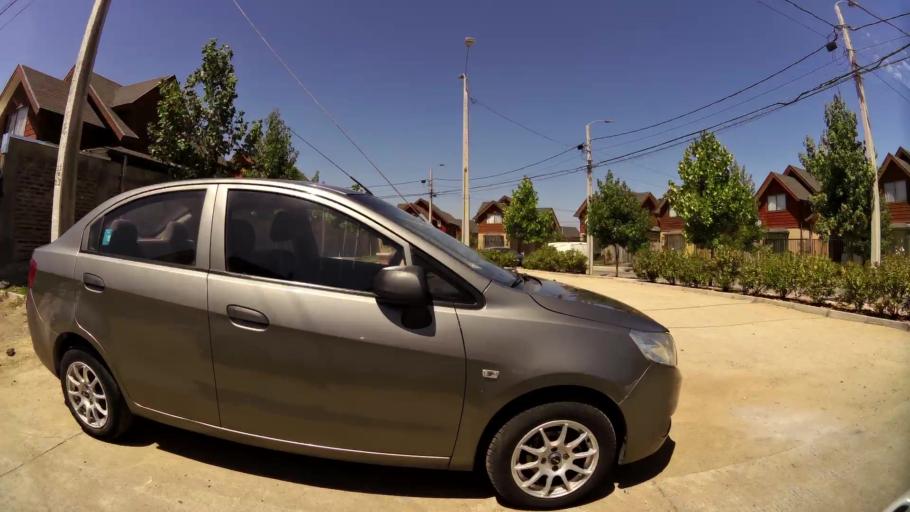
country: CL
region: Maule
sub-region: Provincia de Talca
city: Talca
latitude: -35.4276
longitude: -71.6188
